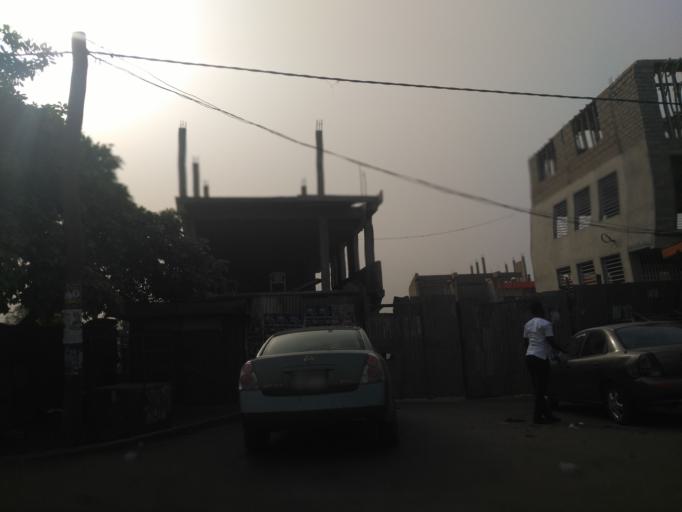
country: GH
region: Ashanti
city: Tafo
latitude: 6.7220
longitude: -1.6333
